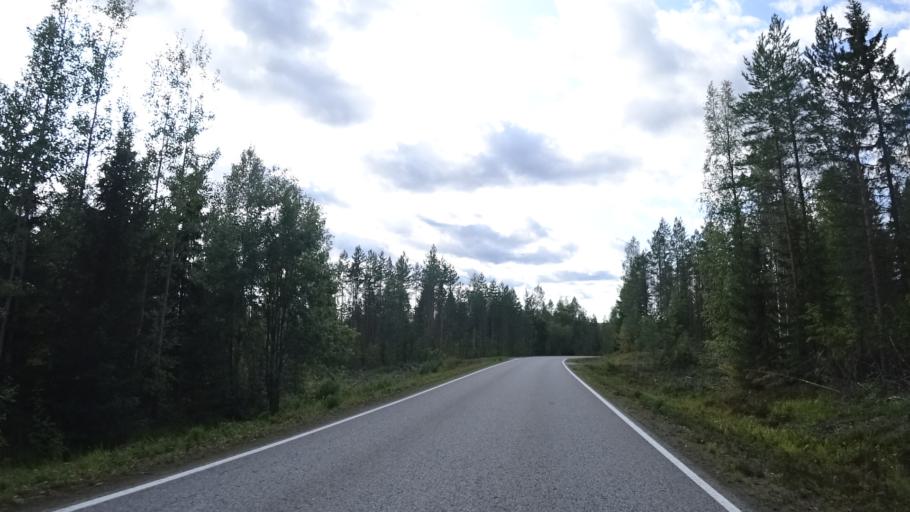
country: RU
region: Republic of Karelia
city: Vyartsilya
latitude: 62.2221
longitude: 30.6434
